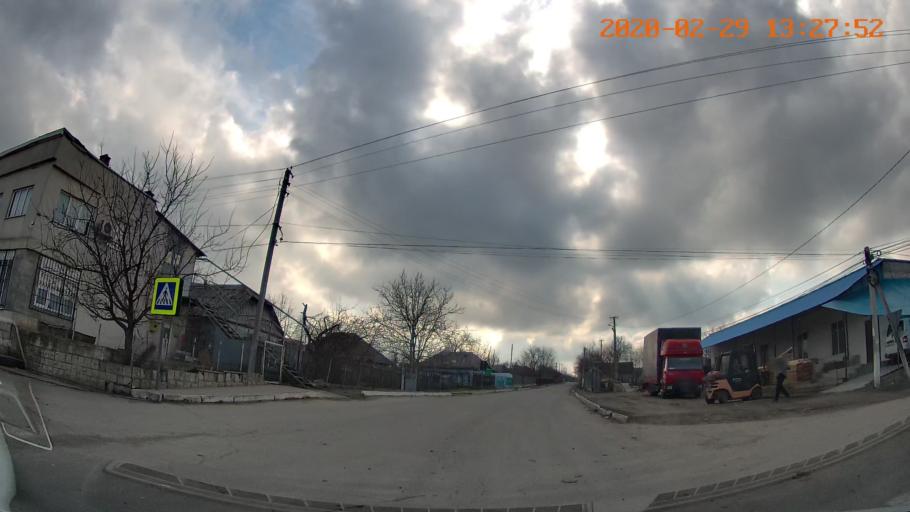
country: MD
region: Telenesti
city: Camenca
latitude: 47.9097
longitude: 28.6450
